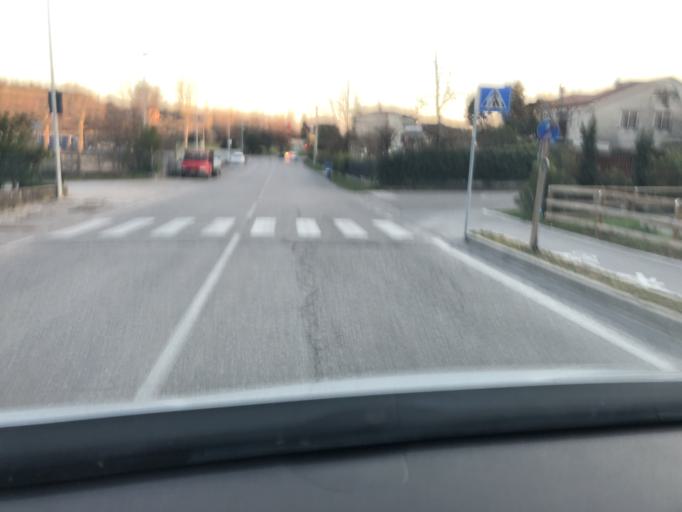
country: IT
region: Veneto
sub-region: Provincia di Verona
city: Sona
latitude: 45.4448
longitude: 10.8209
